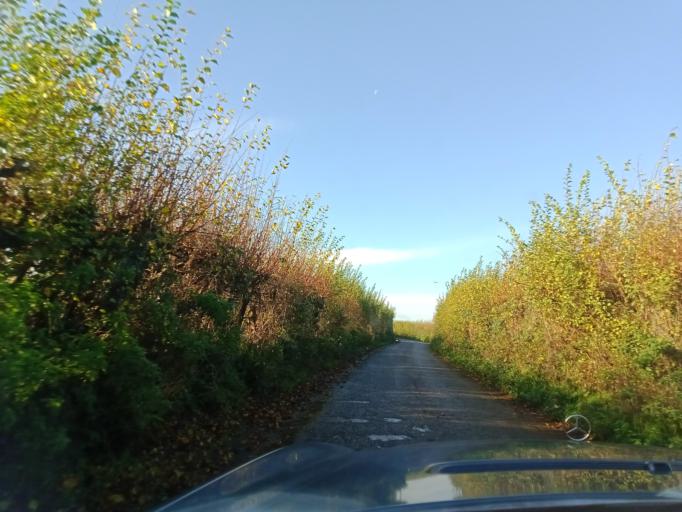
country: IE
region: Leinster
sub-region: Kilkenny
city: Mooncoin
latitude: 52.3001
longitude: -7.2126
